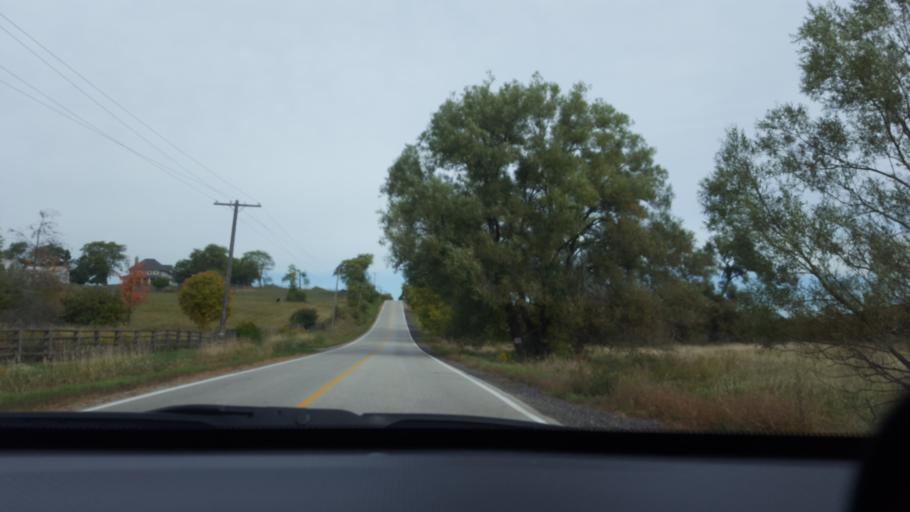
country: CA
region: Ontario
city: Newmarket
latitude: 44.0079
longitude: -79.5491
